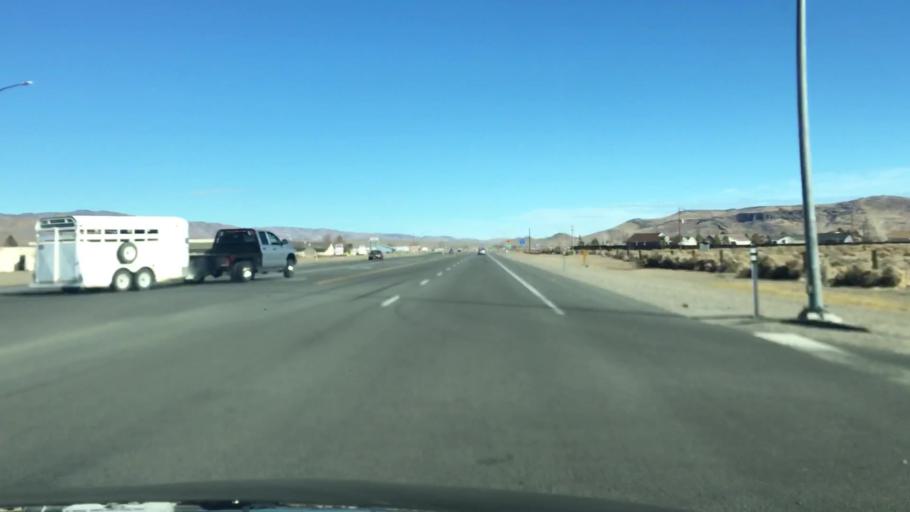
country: US
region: Nevada
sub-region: Lyon County
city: Dayton
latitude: 39.2936
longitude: -119.5314
